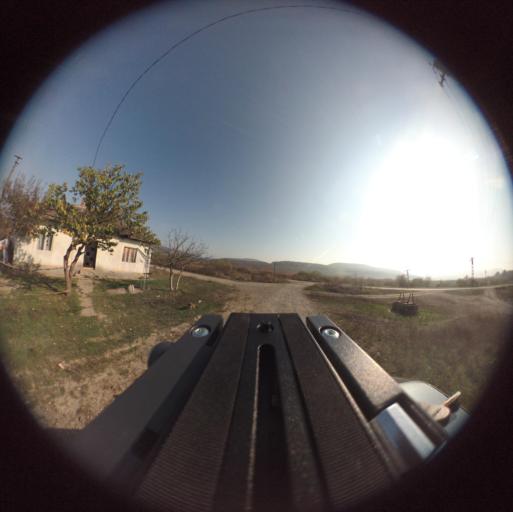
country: RO
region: Vaslui
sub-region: Comuna Bacesti
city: Bacesti
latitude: 46.8279
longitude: 27.2554
